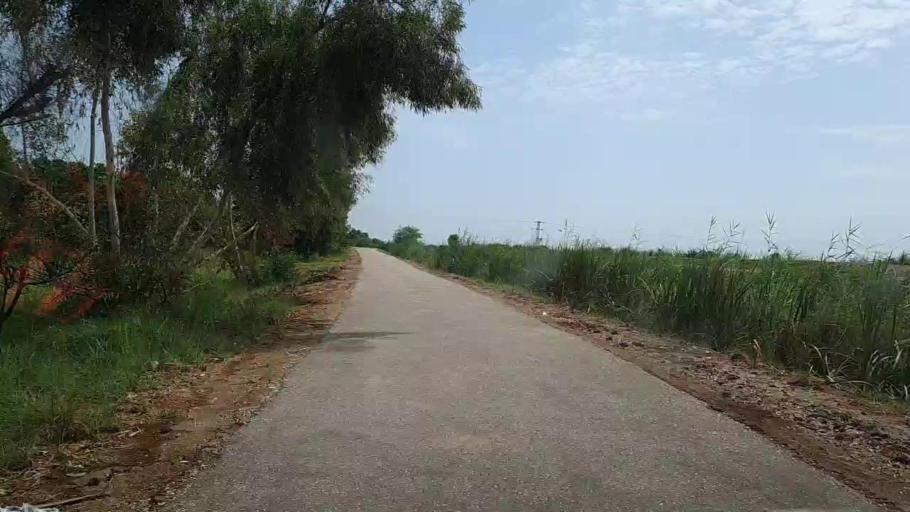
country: PK
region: Sindh
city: Bhiria
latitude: 26.9038
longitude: 68.2003
